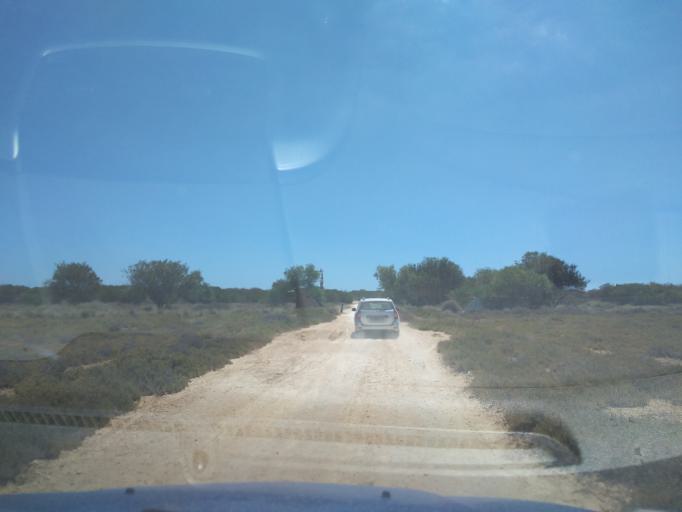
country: TN
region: Susah
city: Harqalah
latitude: 36.1626
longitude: 10.4612
